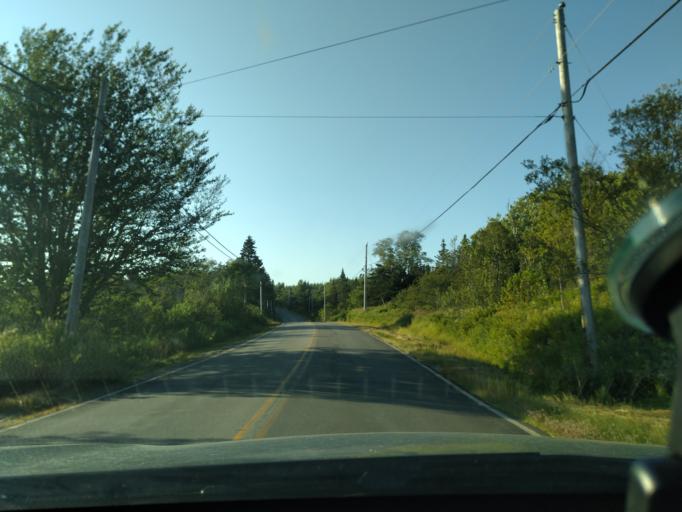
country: US
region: Maine
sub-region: Washington County
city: Machiasport
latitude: 44.6659
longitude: -67.2382
